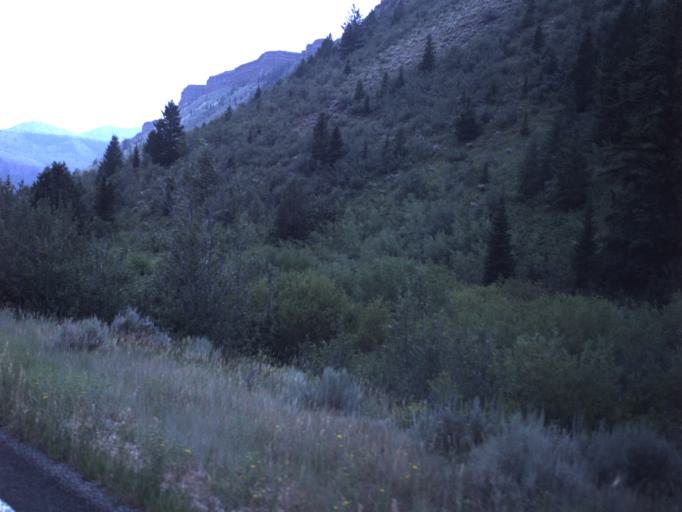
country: US
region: Utah
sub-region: Summit County
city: Francis
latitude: 40.4707
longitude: -110.9056
